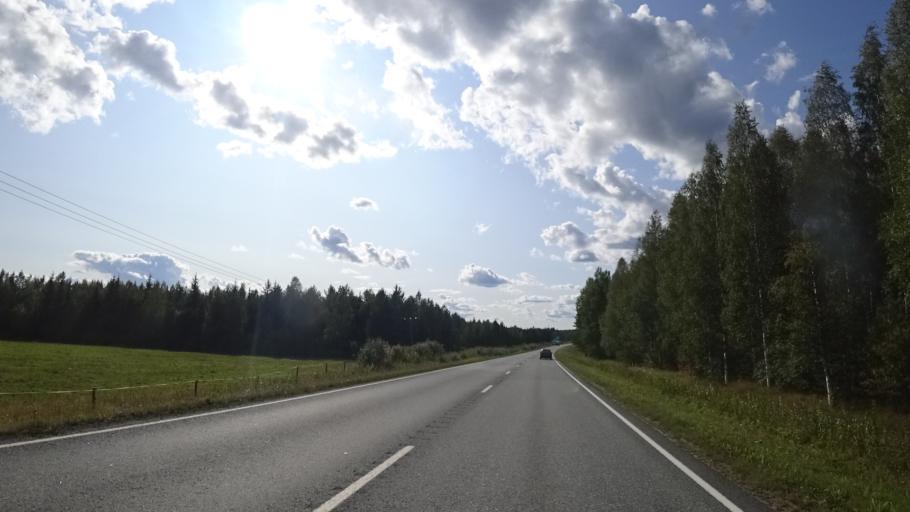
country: FI
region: North Karelia
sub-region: Keski-Karjala
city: Kitee
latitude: 62.0883
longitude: 29.9964
